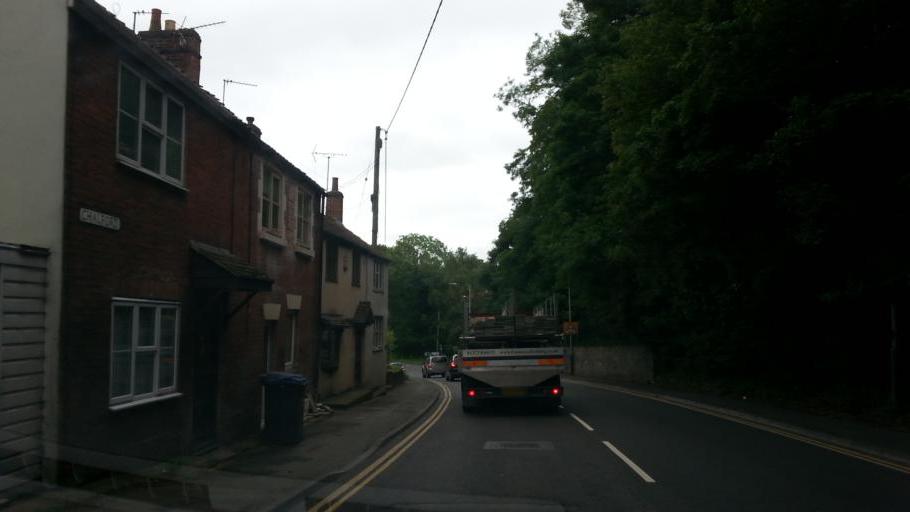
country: GB
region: England
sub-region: Wiltshire
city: Westbury
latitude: 51.2515
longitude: -2.1895
